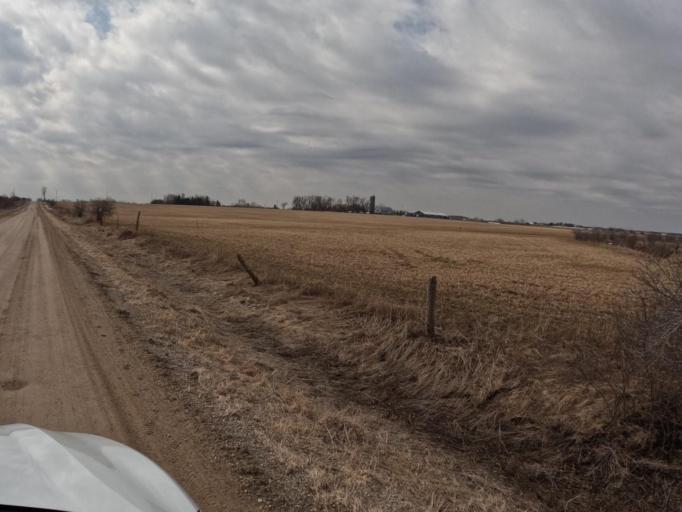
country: CA
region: Ontario
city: Orangeville
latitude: 43.9258
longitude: -80.2192
